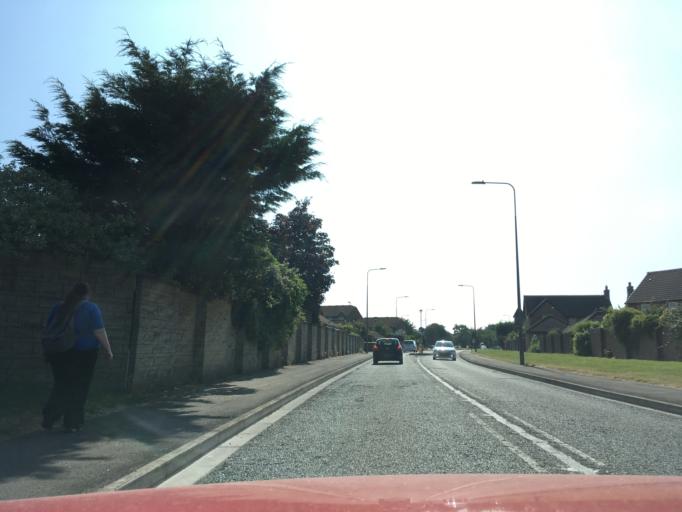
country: GB
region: England
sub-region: South Gloucestershire
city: Stoke Gifford
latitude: 51.5258
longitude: -2.5437
